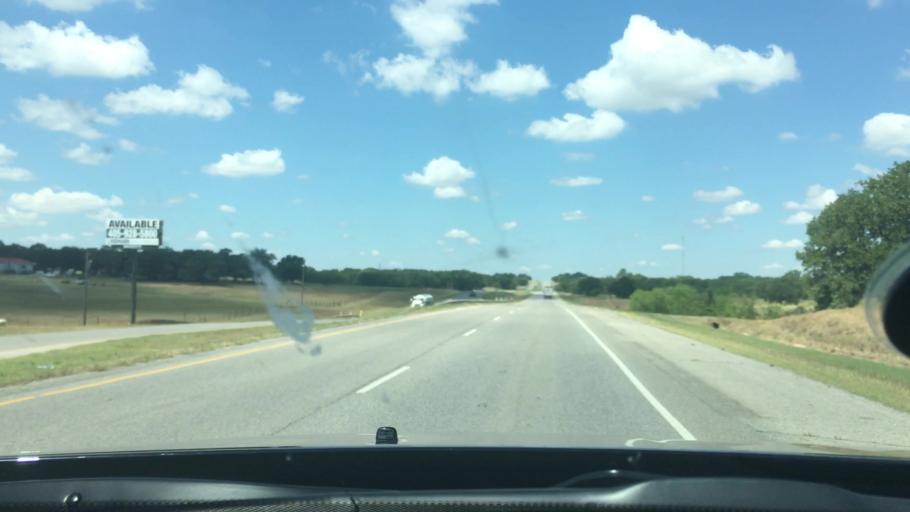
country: US
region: Oklahoma
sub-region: Carter County
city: Wilson
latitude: 34.1730
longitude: -97.3876
